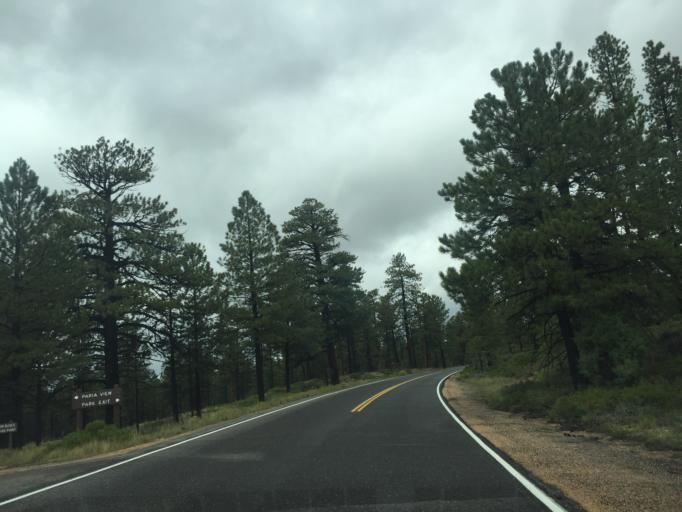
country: US
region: Utah
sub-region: Garfield County
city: Panguitch
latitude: 37.6009
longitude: -112.1652
